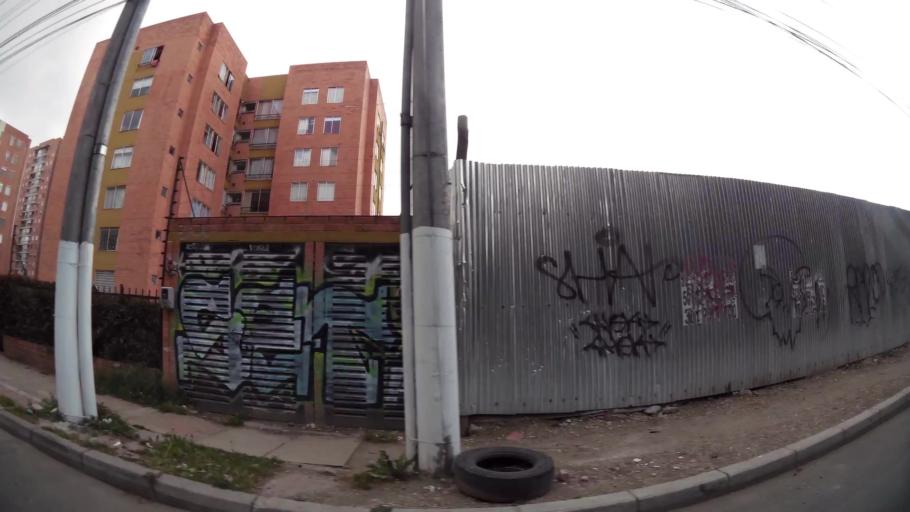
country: CO
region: Cundinamarca
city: Cota
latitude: 4.7417
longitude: -74.0572
